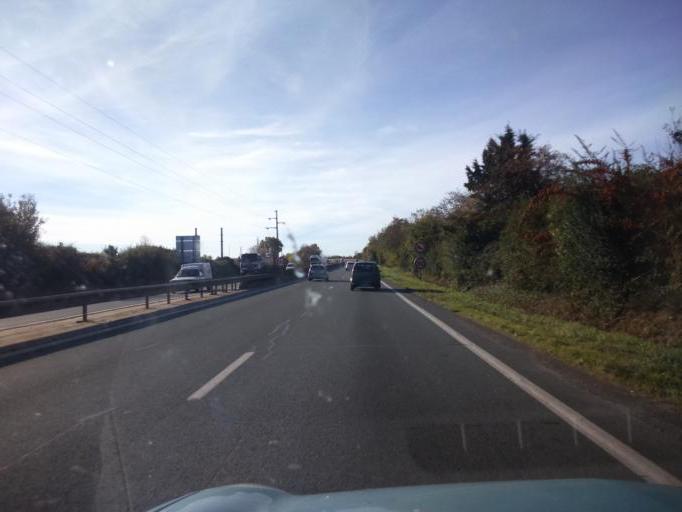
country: FR
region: Poitou-Charentes
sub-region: Departement de la Charente-Maritime
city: Puilboreau
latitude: 46.1665
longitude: -1.1215
